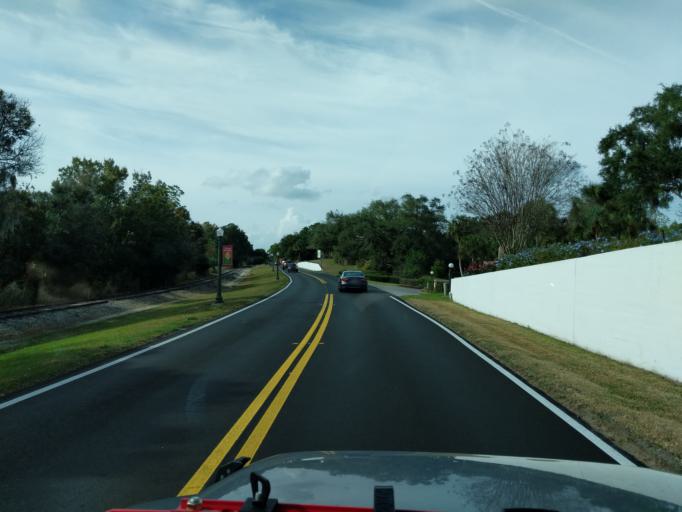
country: US
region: Florida
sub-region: Lake County
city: Mount Dora
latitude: 28.8032
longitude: -81.6497
